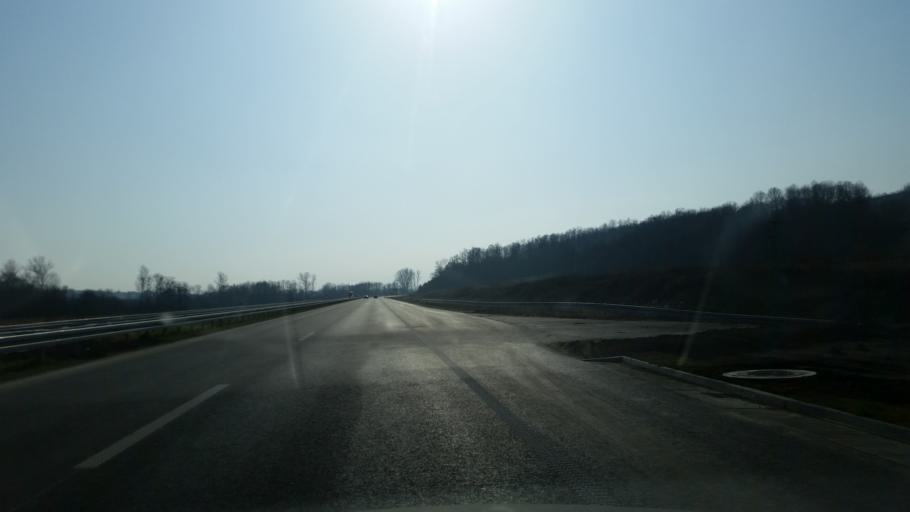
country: RS
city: Prislonica
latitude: 43.9341
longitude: 20.4011
